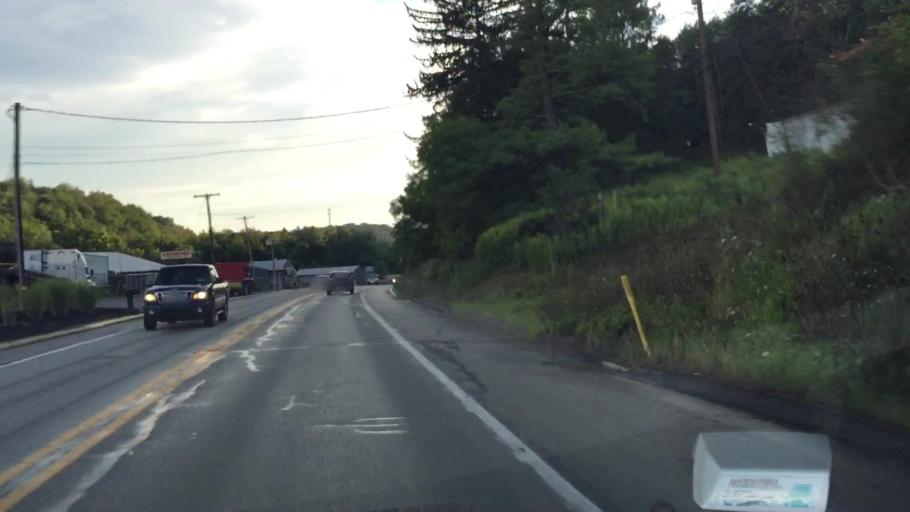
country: US
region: Pennsylvania
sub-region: Butler County
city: Evans City
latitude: 40.7769
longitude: -80.0505
